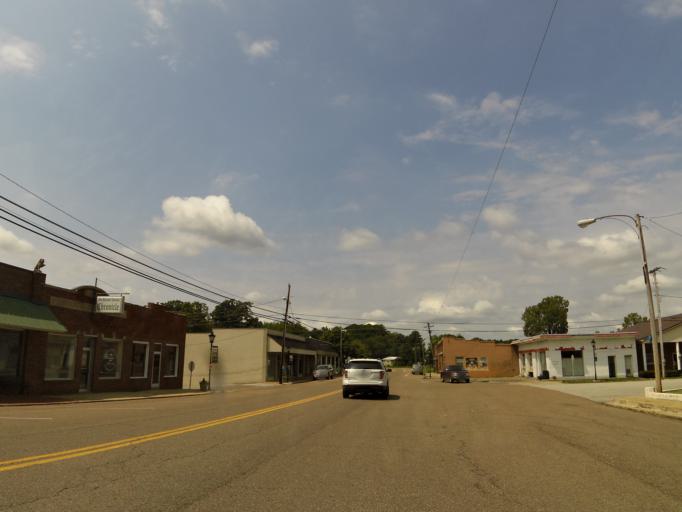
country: US
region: Tennessee
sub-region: Decatur County
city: Decaturville
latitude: 35.5842
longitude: -88.1201
